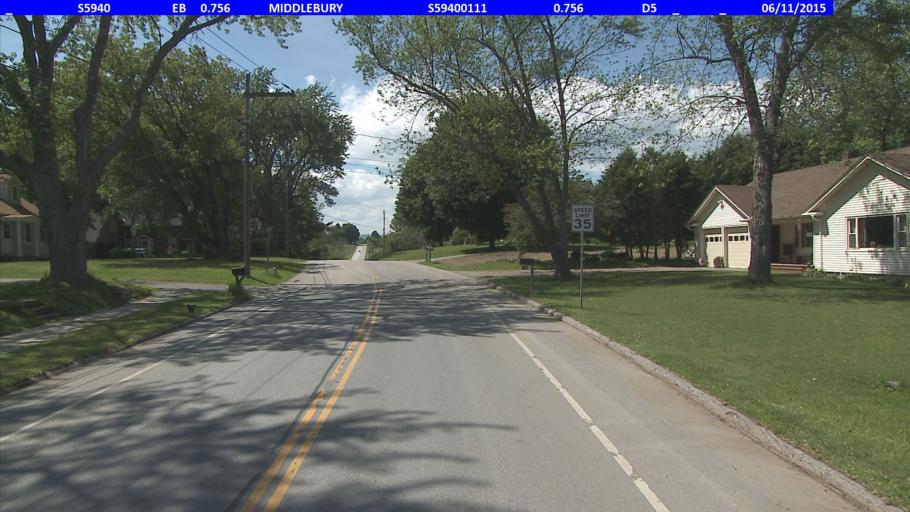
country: US
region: Vermont
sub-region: Addison County
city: Middlebury (village)
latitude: 44.0194
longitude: -73.1818
